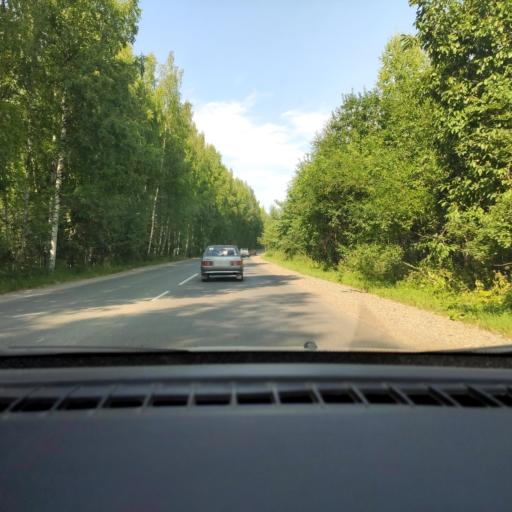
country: RU
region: Perm
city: Polazna
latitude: 58.1203
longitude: 56.4310
